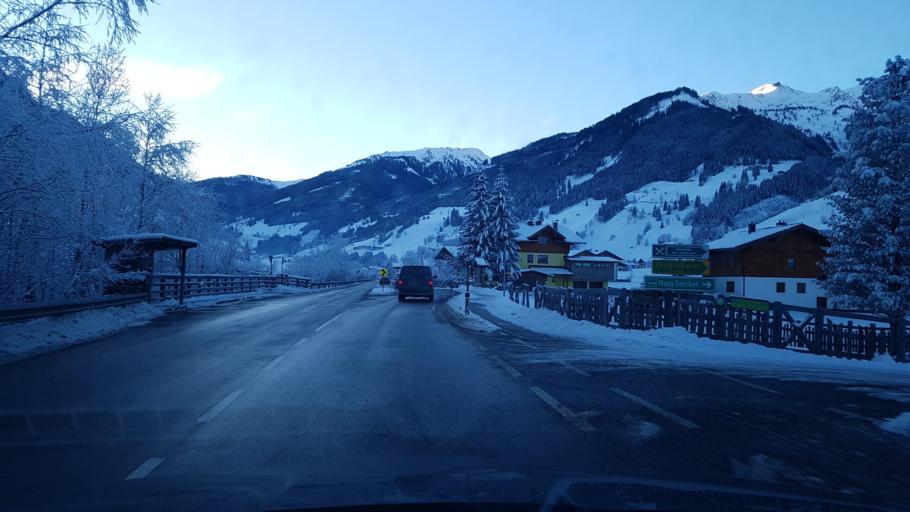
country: AT
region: Salzburg
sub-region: Politischer Bezirk Sankt Johann im Pongau
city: Huttschlag
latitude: 47.2210
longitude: 13.1968
